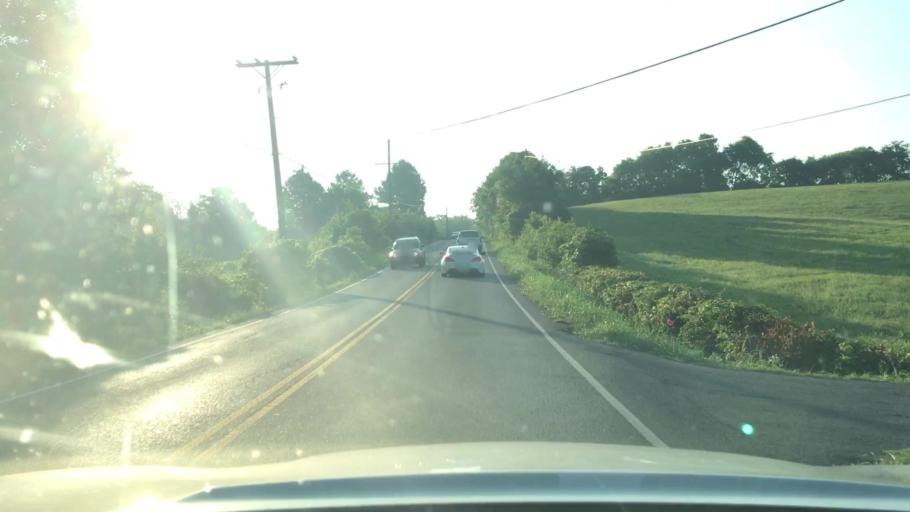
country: US
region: Tennessee
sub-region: Williamson County
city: Nolensville
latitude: 35.9915
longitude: -86.6495
